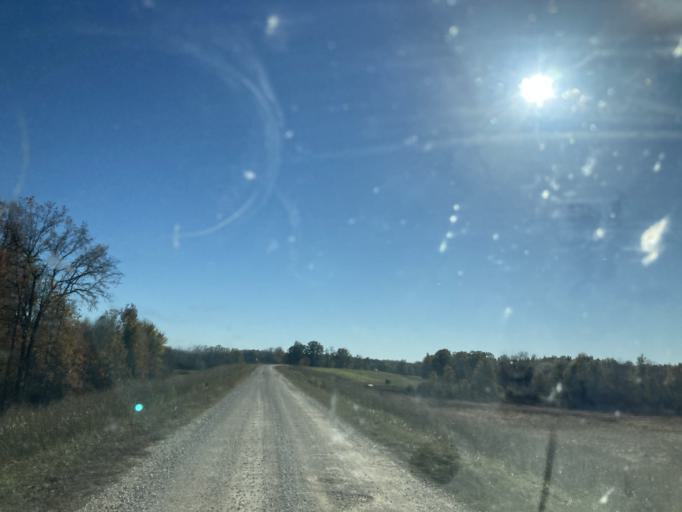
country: US
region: Mississippi
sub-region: Sharkey County
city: Rolling Fork
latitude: 32.7050
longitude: -90.6802
